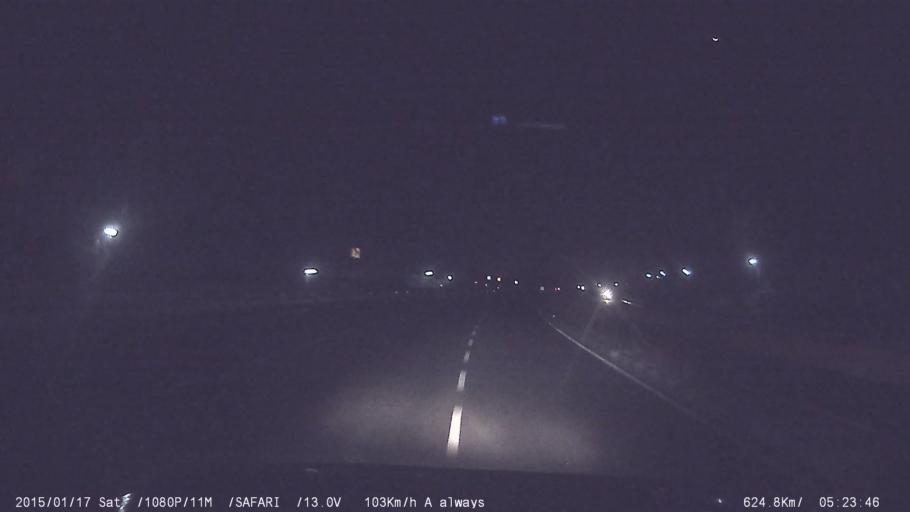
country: IN
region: Tamil Nadu
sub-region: Vellore
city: Katpadi
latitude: 12.9468
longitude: 79.2048
